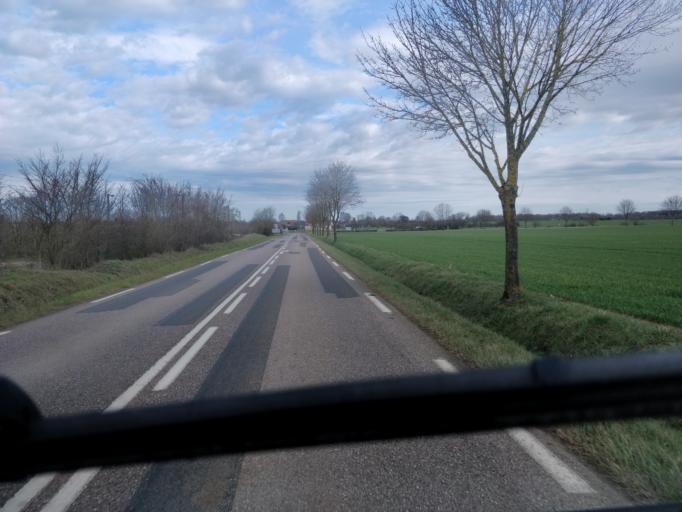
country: FR
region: Lorraine
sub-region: Departement de Meurthe-et-Moselle
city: Doncourt-les-Conflans
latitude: 49.0891
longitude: 5.8926
